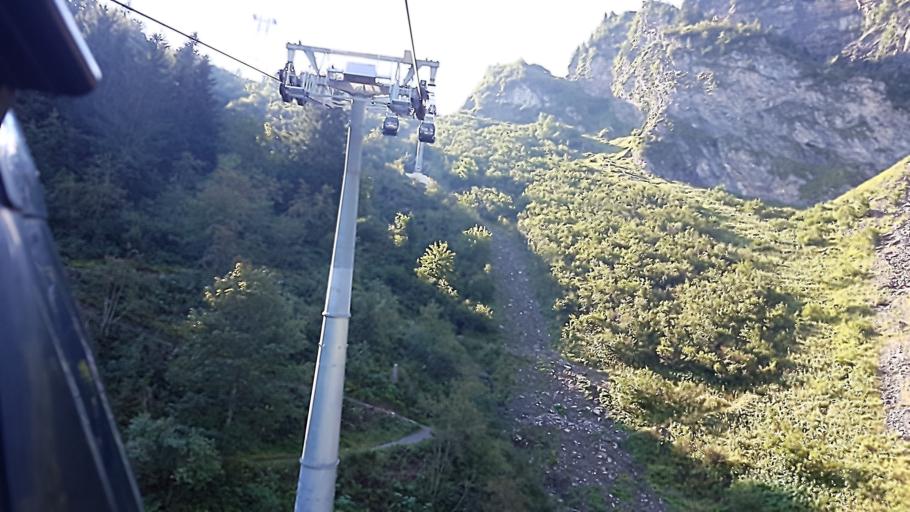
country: CH
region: Obwalden
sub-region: Obwalden
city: Engelberg
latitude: 46.7976
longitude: 8.3977
